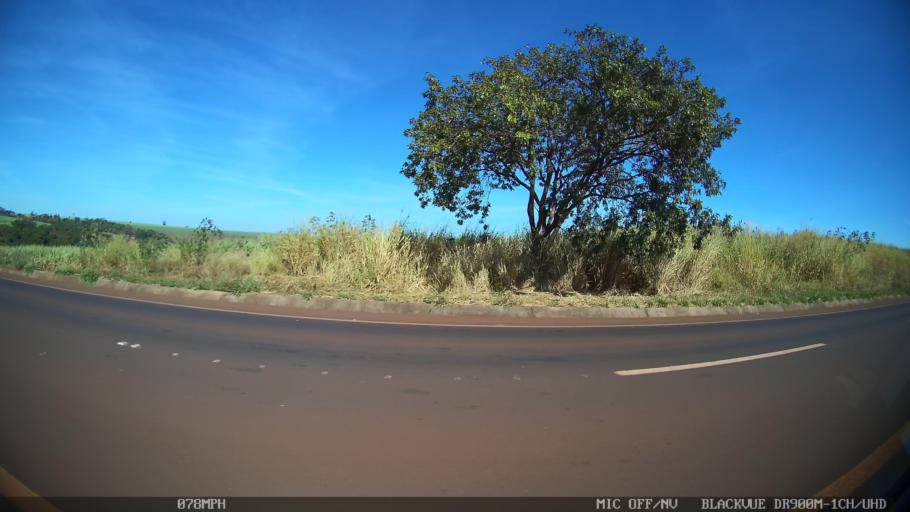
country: BR
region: Sao Paulo
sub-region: Sao Joaquim Da Barra
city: Sao Joaquim da Barra
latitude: -20.5523
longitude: -47.7337
